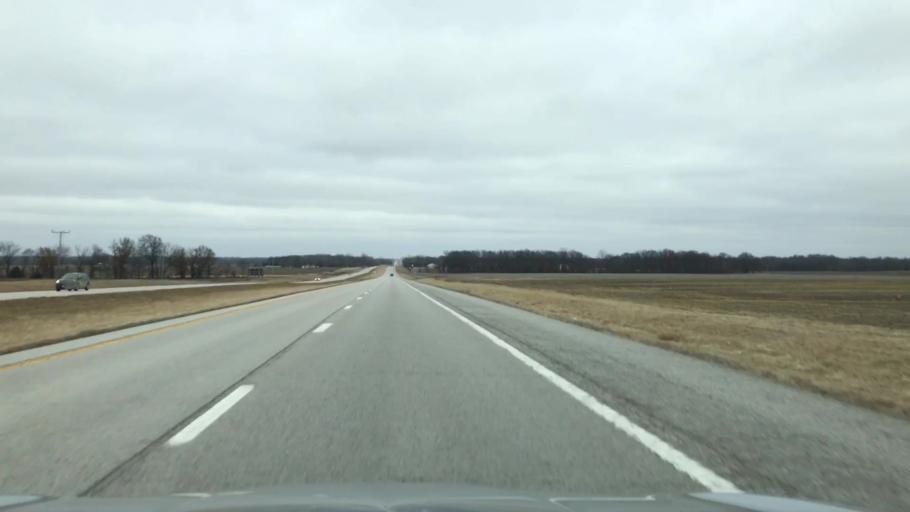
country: US
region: Missouri
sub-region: Livingston County
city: Chillicothe
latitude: 39.7764
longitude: -93.4582
